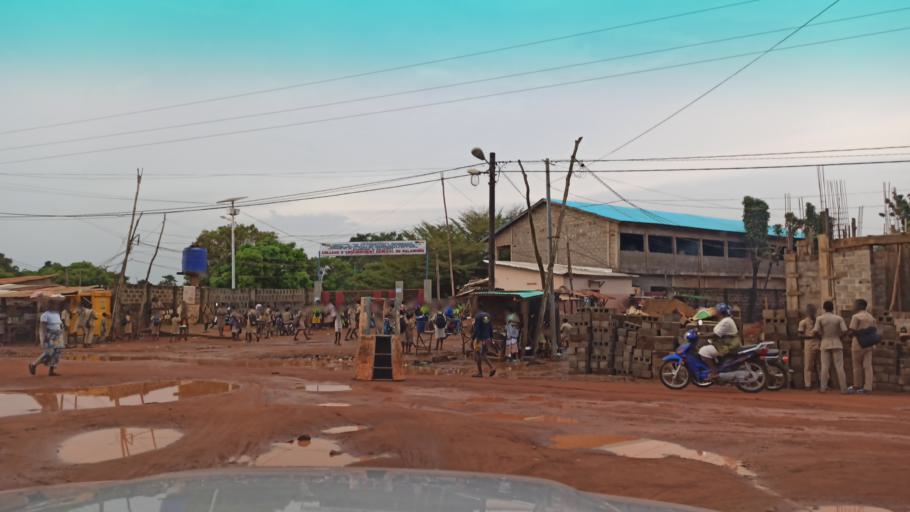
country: BJ
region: Queme
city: Porto-Novo
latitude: 6.4897
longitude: 2.6653
